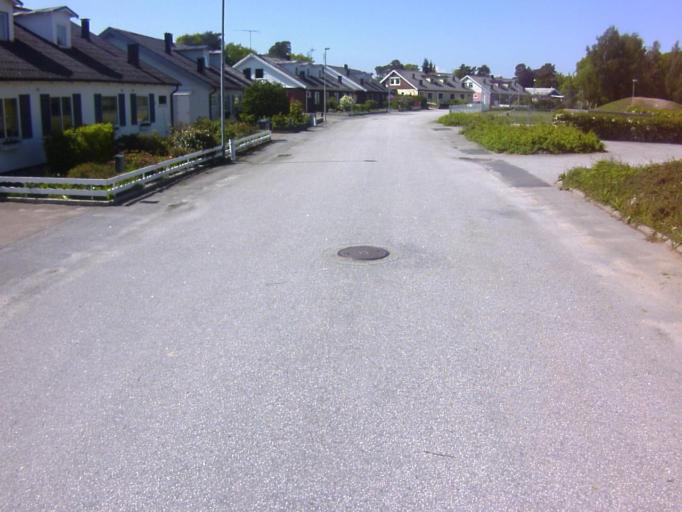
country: SE
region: Blekinge
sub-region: Solvesborgs Kommun
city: Soelvesborg
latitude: 56.0376
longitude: 14.5694
